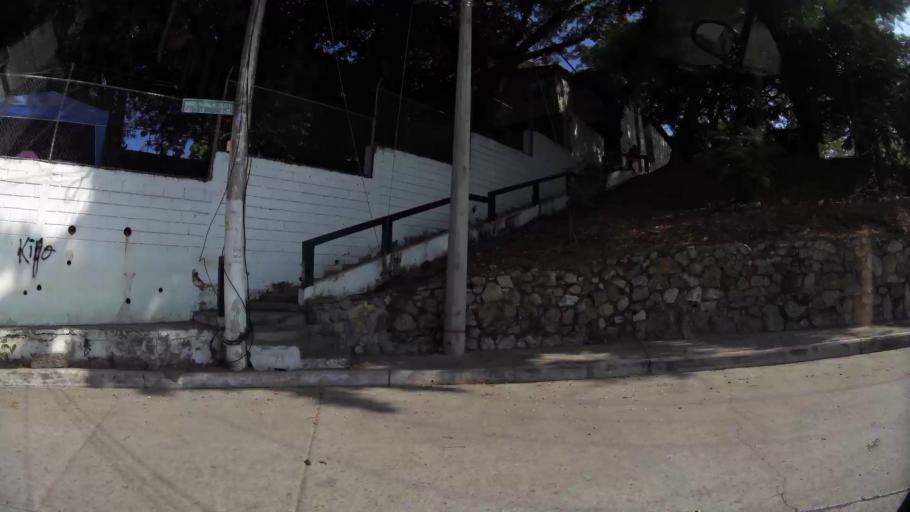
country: EC
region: Guayas
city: Guayaquil
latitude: -2.1628
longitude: -79.9371
